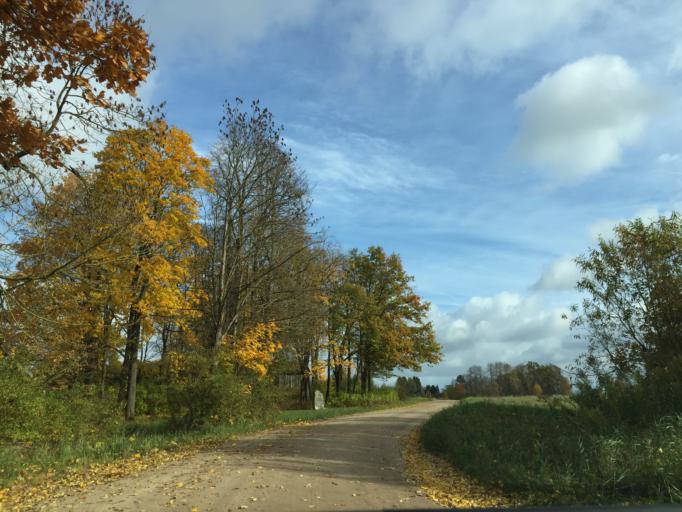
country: LV
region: Lielvarde
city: Lielvarde
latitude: 56.7199
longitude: 24.8308
